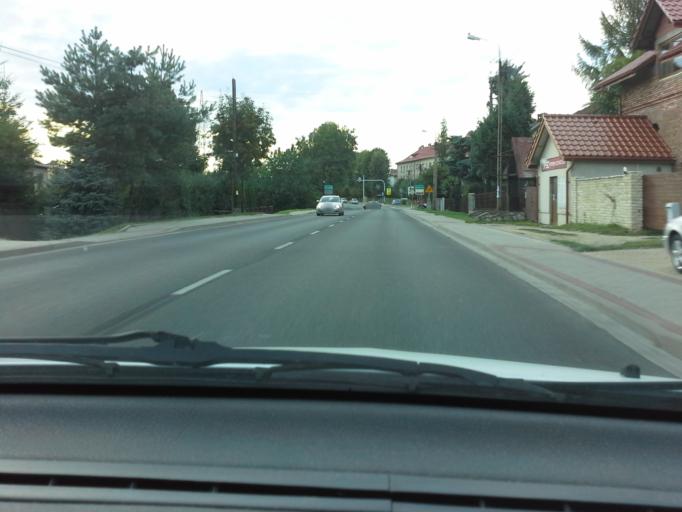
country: PL
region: Lesser Poland Voivodeship
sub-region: Powiat chrzanowski
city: Trzebinia
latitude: 50.1554
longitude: 19.4813
